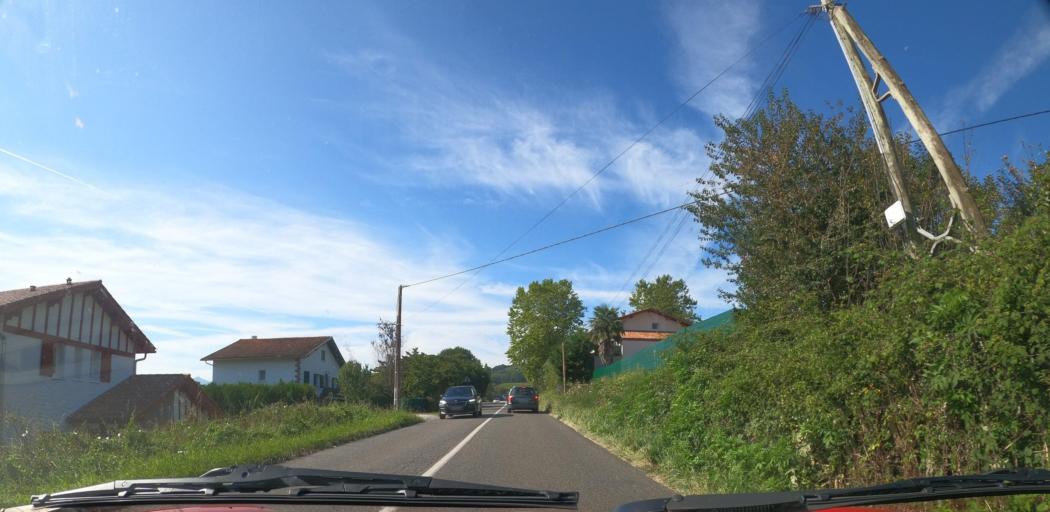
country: FR
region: Aquitaine
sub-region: Departement des Pyrenees-Atlantiques
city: Saint-Pee-sur-Nivelle
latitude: 43.3403
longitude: -1.5497
